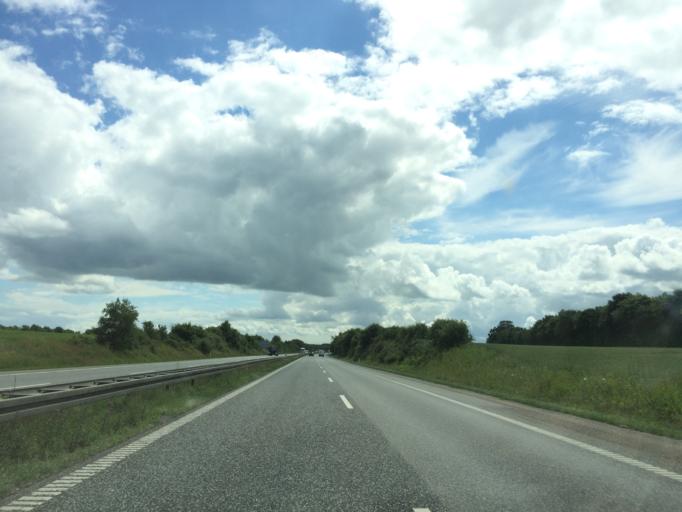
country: DK
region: North Denmark
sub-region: Mariagerfjord Kommune
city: Hobro
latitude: 56.6603
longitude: 9.7355
